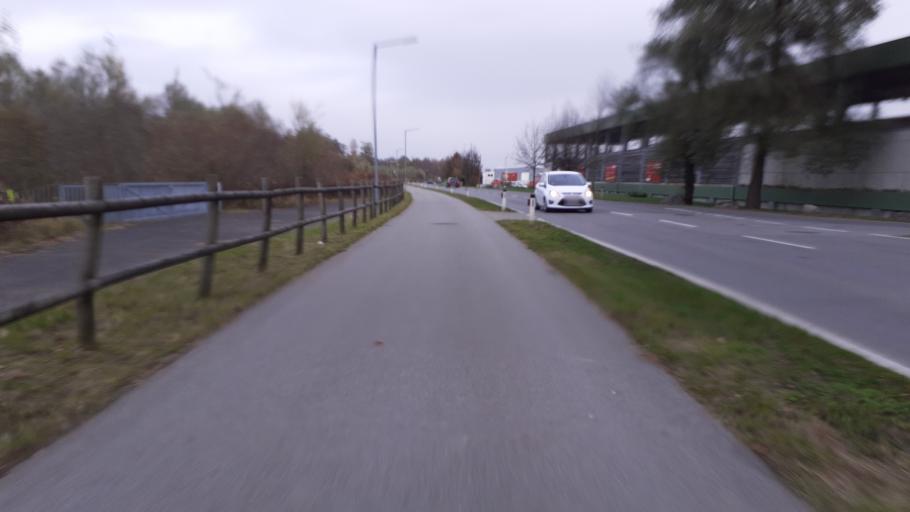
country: AT
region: Vorarlberg
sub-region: Politischer Bezirk Feldkirch
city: Nofels
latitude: 47.2709
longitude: 9.5907
